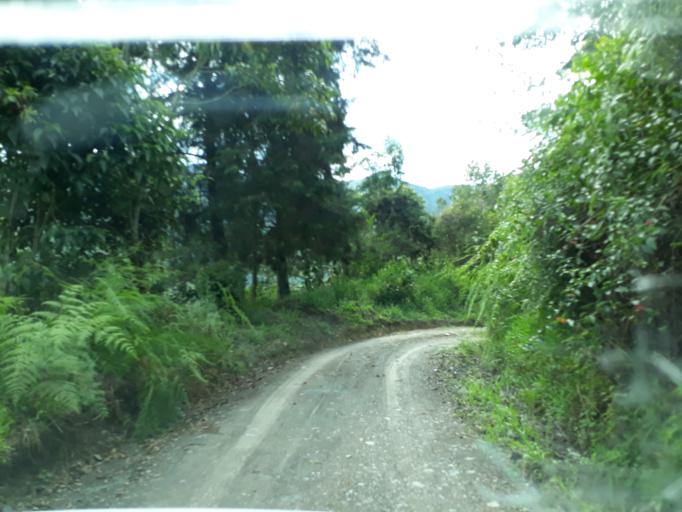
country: CO
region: Cundinamarca
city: Pacho
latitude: 5.1718
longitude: -74.2450
